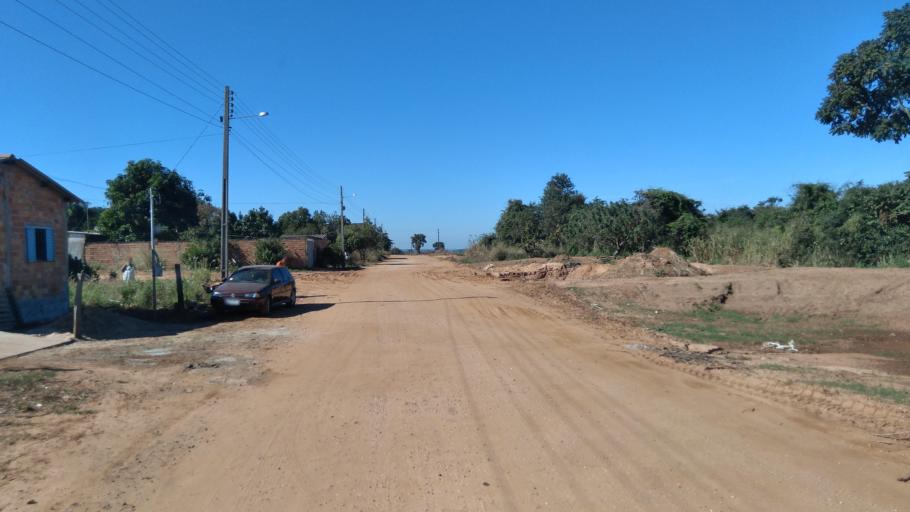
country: BR
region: Goias
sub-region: Mineiros
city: Mineiros
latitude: -17.5920
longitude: -52.5586
